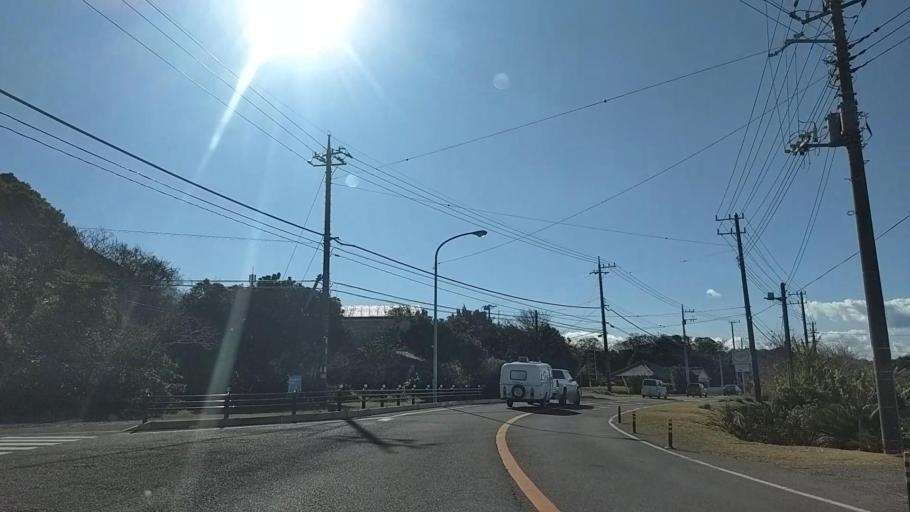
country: JP
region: Chiba
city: Tateyama
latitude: 34.9387
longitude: 139.8419
